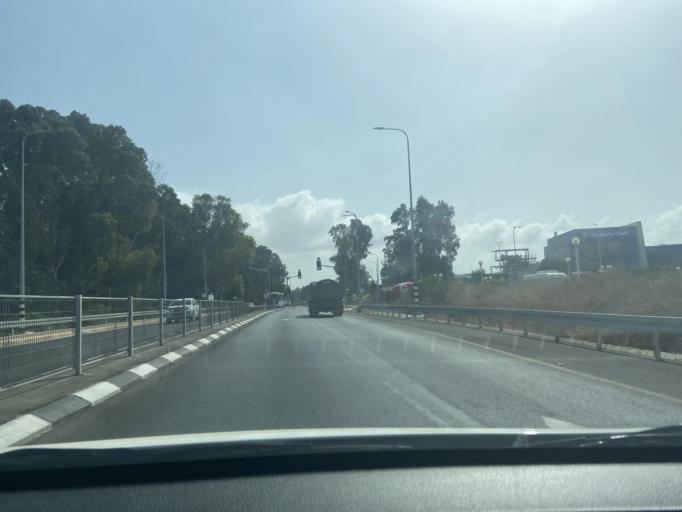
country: IL
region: Northern District
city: Nahariya
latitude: 33.0420
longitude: 35.1066
